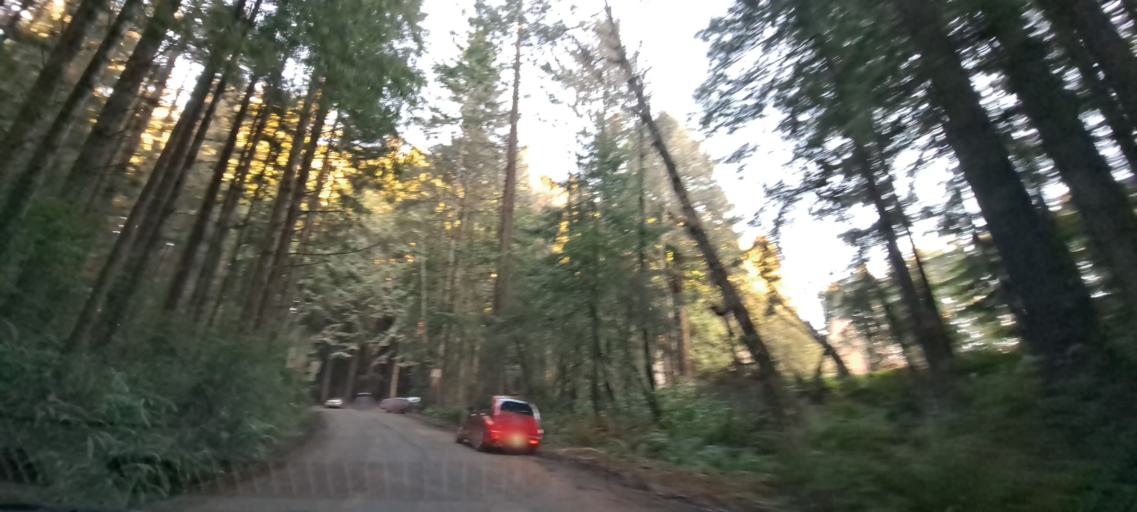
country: US
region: California
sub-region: Humboldt County
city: Arcata
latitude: 40.8700
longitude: -124.0730
